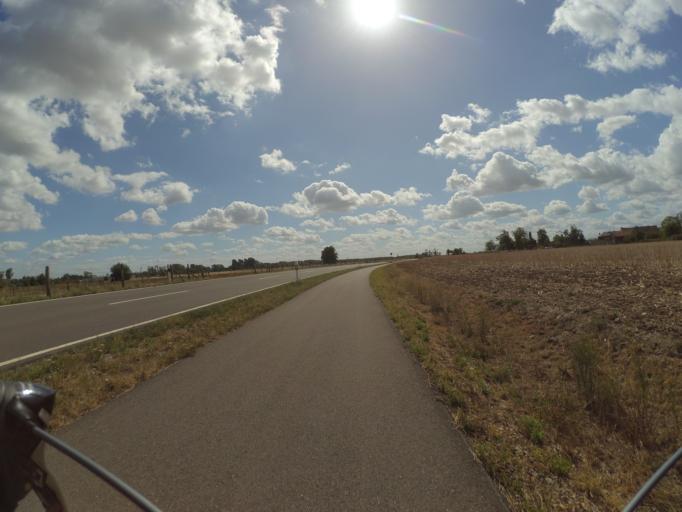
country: DE
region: North Rhine-Westphalia
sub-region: Regierungsbezirk Koln
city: Inden
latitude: 50.8888
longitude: 6.3780
